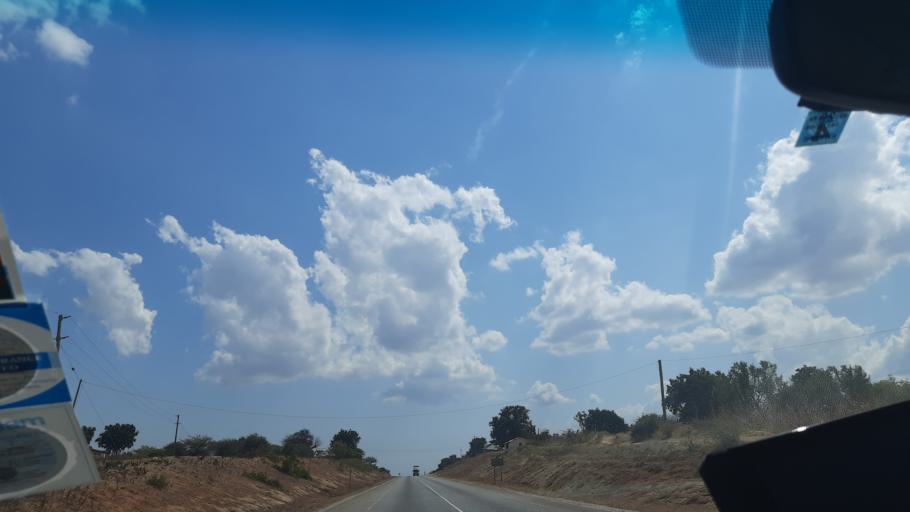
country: TZ
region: Singida
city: Kintinku
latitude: -6.0145
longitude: 35.4377
